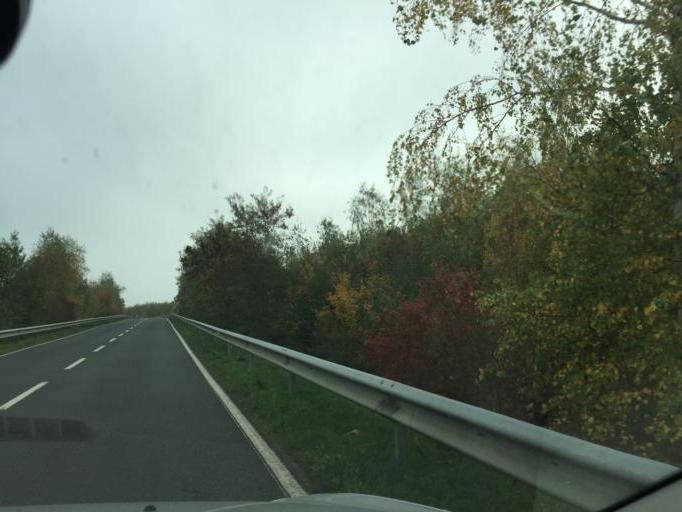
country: LU
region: Luxembourg
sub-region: Canton de Luxembourg
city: Sandweiler
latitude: 49.6103
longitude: 6.2030
